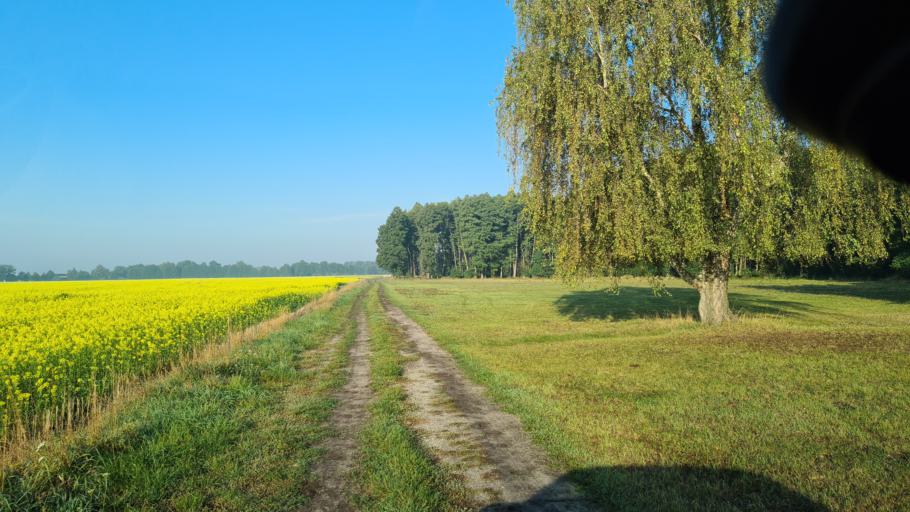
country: DE
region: Brandenburg
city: Schonewalde
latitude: 51.6576
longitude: 13.6156
